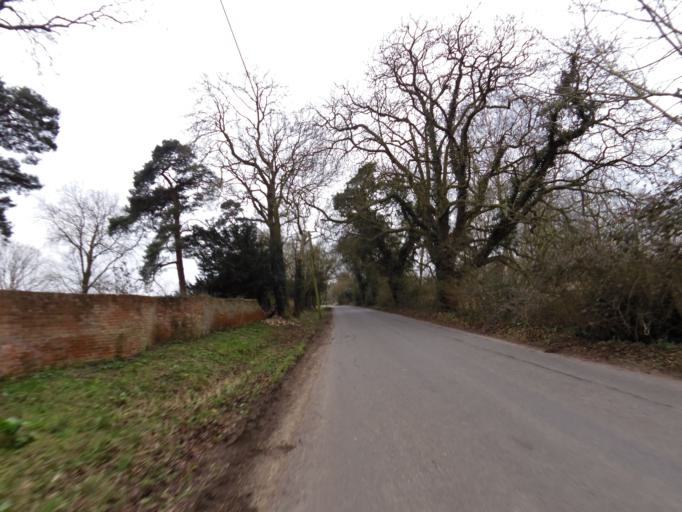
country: GB
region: England
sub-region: Suffolk
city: Framlingham
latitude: 52.1869
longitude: 1.3354
